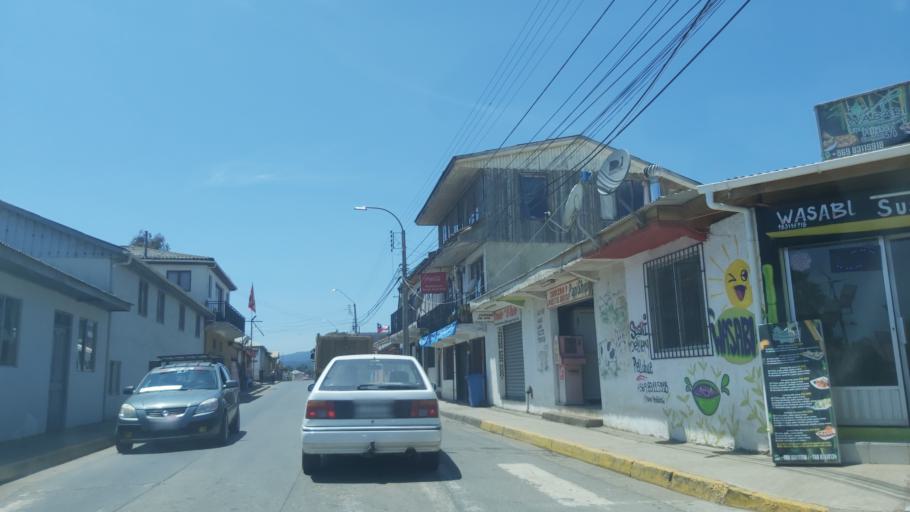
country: CL
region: Maule
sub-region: Provincia de Cauquenes
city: Cauquenes
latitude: -35.8153
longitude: -72.5765
